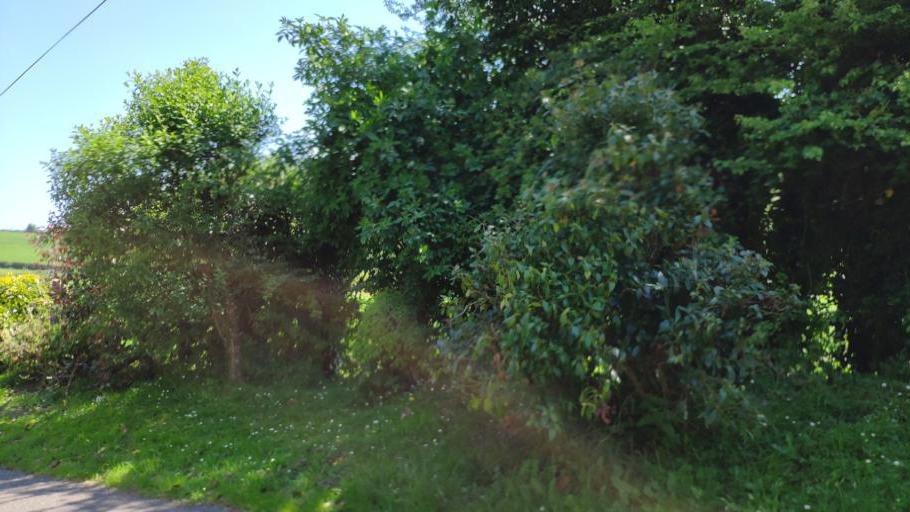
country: IE
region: Munster
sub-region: County Cork
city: Cork
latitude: 51.9169
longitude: -8.5153
